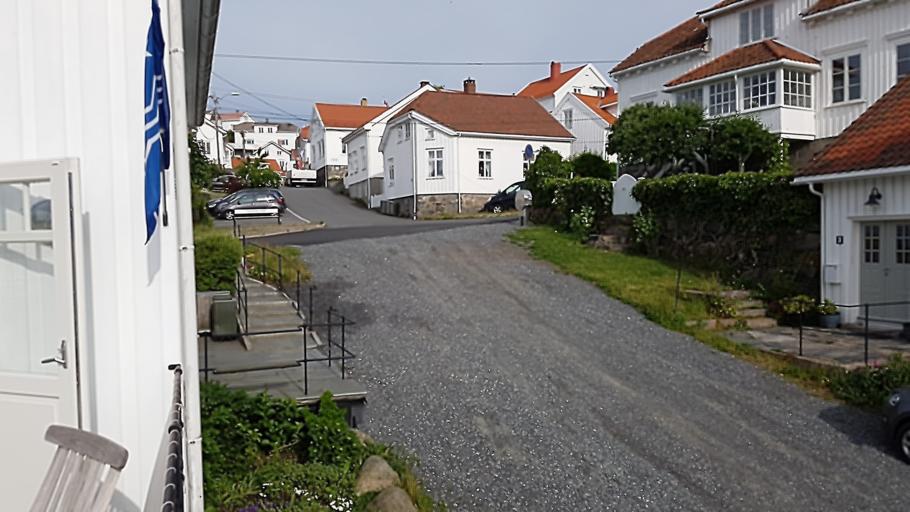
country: NO
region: Aust-Agder
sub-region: Risor
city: Risor
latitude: 58.7179
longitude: 9.2395
